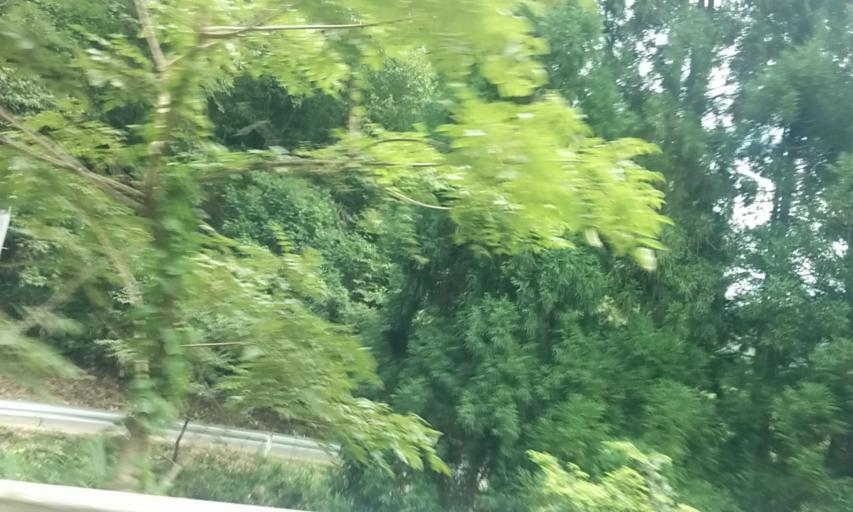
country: JP
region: Kyoto
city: Maizuru
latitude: 35.3538
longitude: 135.3422
